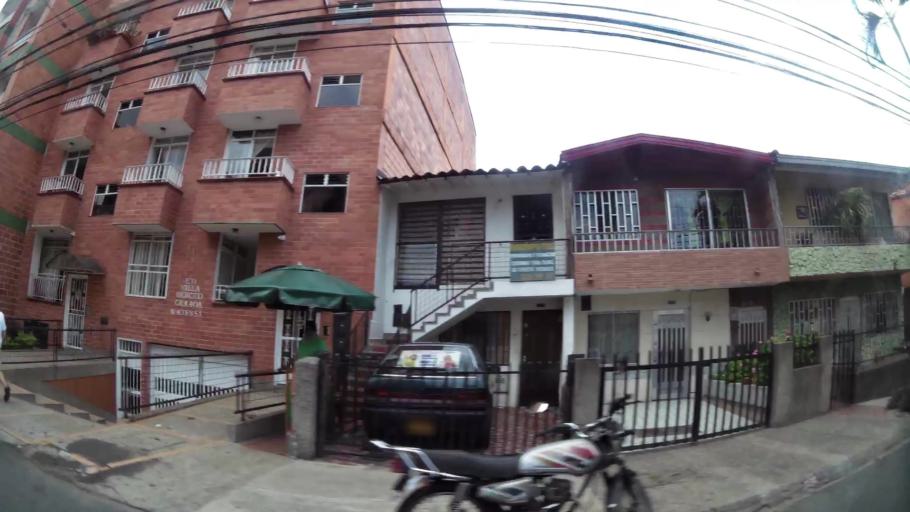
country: CO
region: Antioquia
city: Envigado
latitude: 6.1645
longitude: -75.5899
